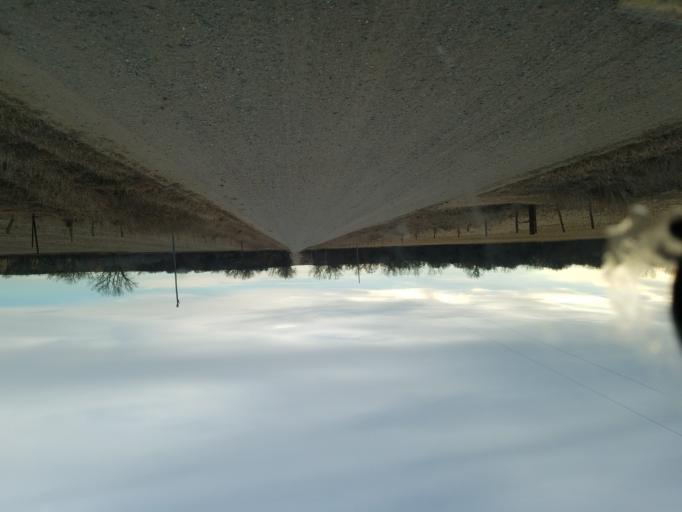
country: US
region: Nebraska
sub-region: Knox County
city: Bloomfield
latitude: 42.5541
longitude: -97.7597
